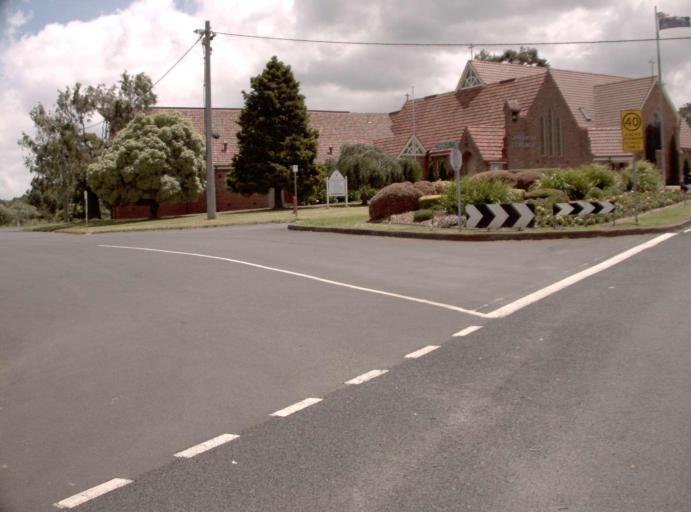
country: AU
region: Victoria
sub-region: Baw Baw
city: Warragul
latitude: -38.1348
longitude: 145.8545
